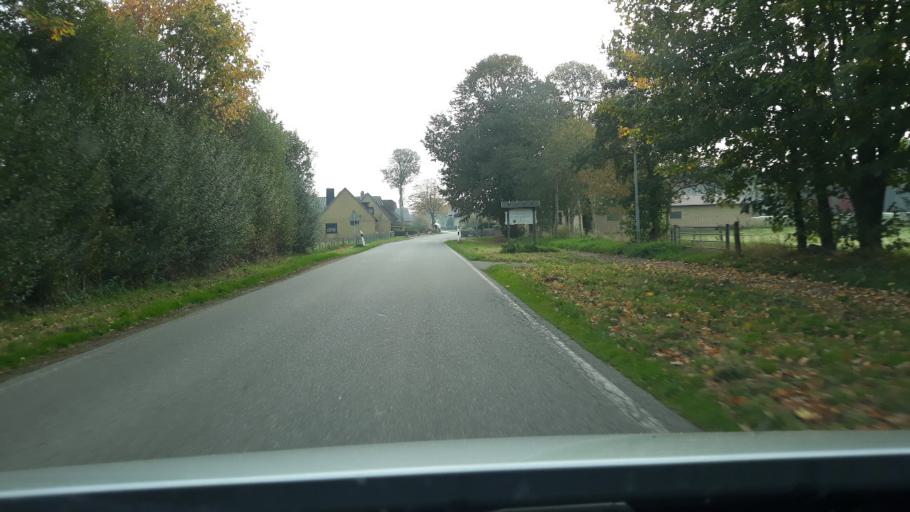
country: DE
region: Schleswig-Holstein
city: Klein Bennebek
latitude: 54.4015
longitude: 9.4461
